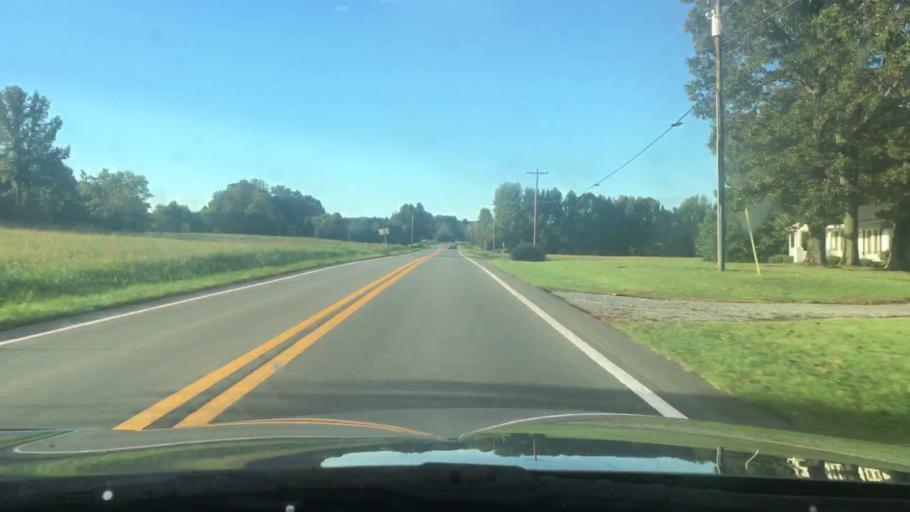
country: US
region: North Carolina
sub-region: Alamance County
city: Green Level
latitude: 36.2030
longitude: -79.3224
